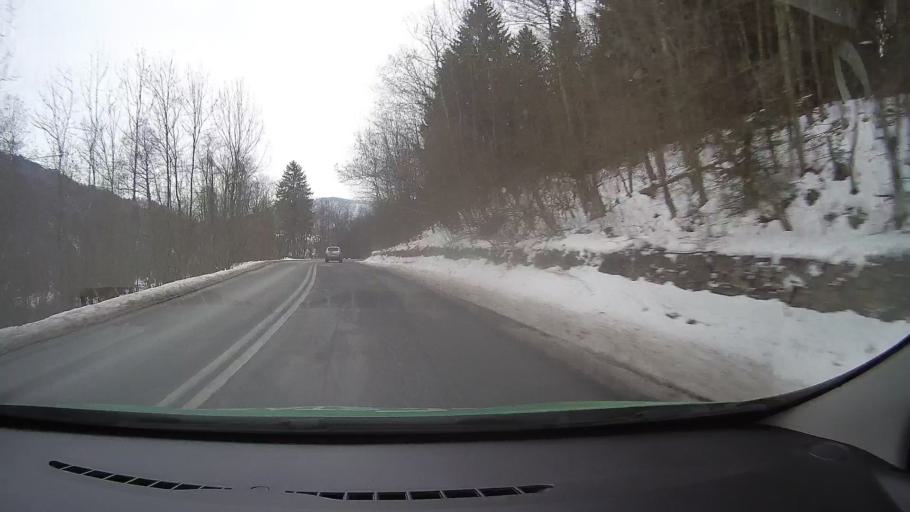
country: RO
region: Brasov
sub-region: Oras Predeal
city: Predeal
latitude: 45.5247
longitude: 25.5039
